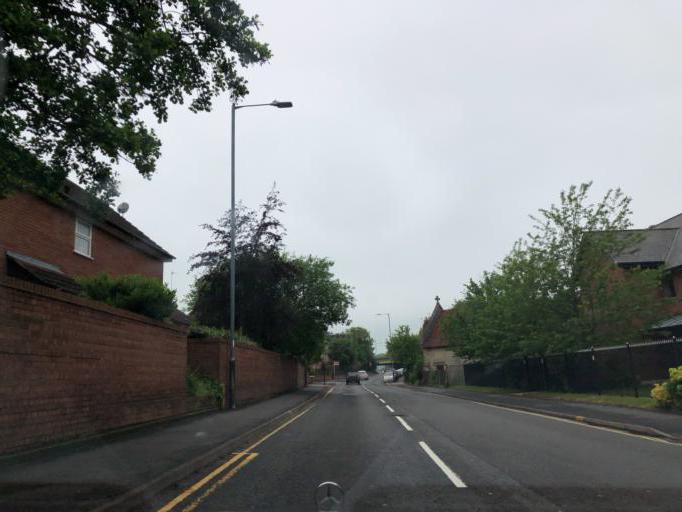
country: GB
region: England
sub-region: Warwickshire
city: Warwick
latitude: 52.2855
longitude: -1.5946
